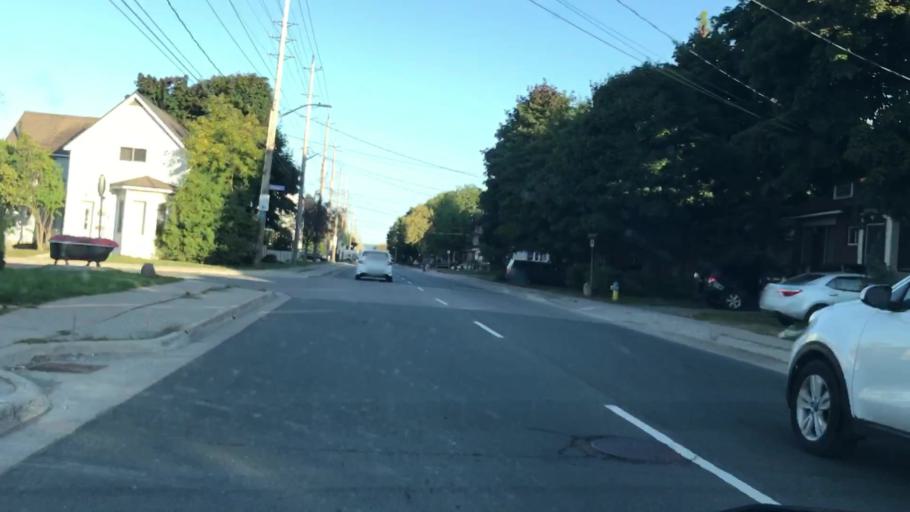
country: CA
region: Ontario
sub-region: Algoma
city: Sault Ste. Marie
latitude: 46.5124
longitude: -84.3292
